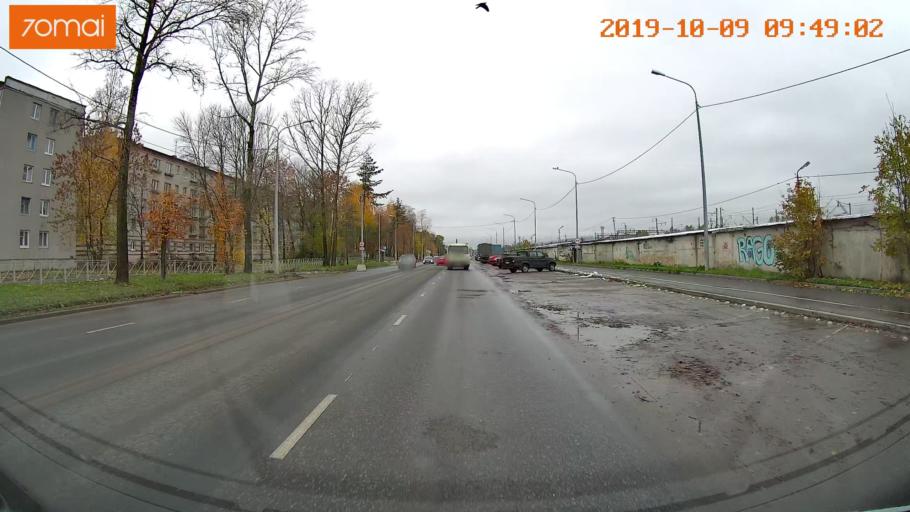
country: RU
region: Vologda
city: Vologda
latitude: 59.1970
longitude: 39.9188
